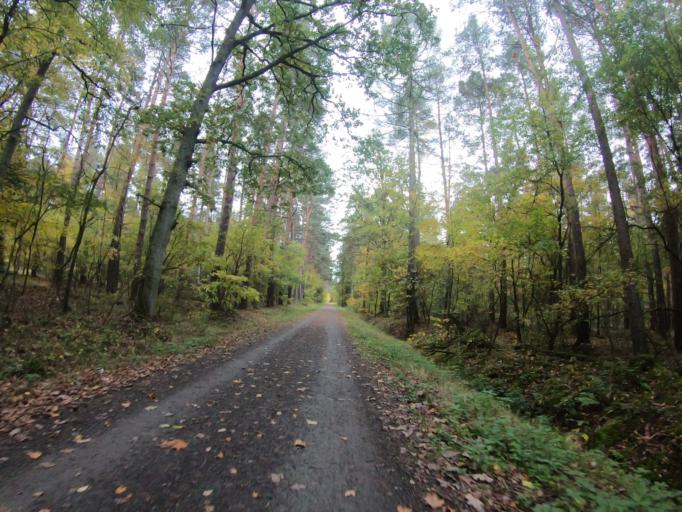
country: DE
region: Lower Saxony
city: Isenbuttel
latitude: 52.4529
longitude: 10.5659
